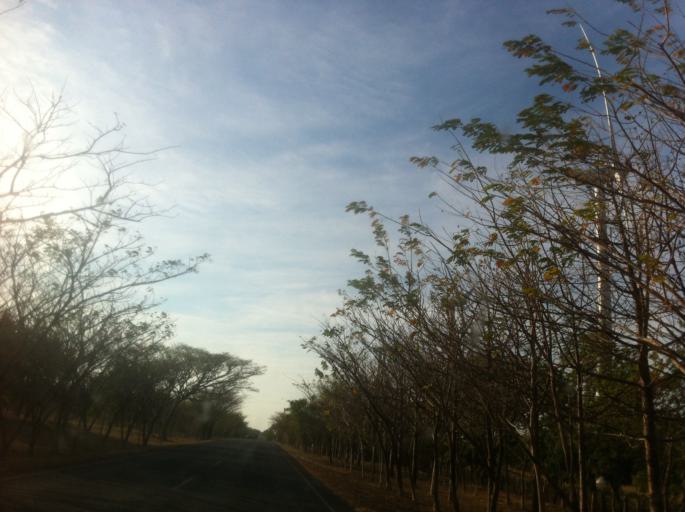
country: NI
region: Rivas
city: Rivas
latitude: 11.3346
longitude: -85.7262
